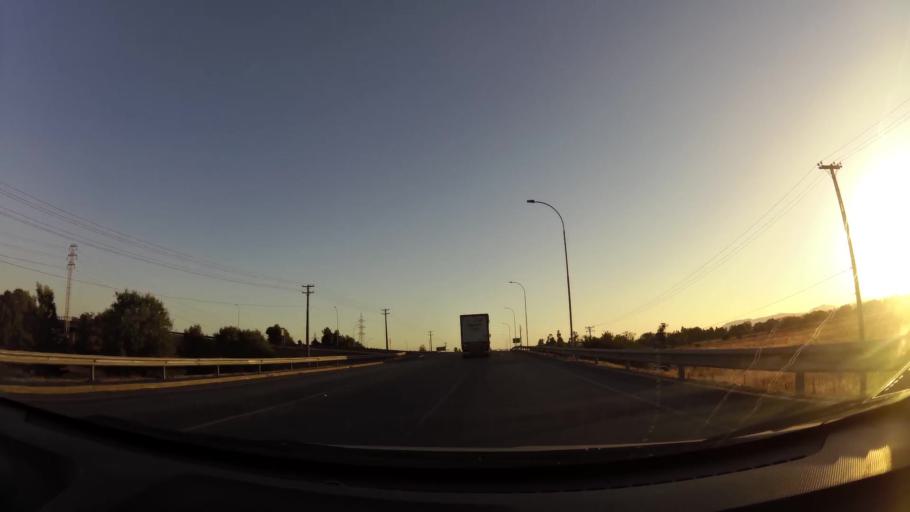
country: CL
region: Maule
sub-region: Provincia de Talca
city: Talca
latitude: -35.4509
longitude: -71.6460
